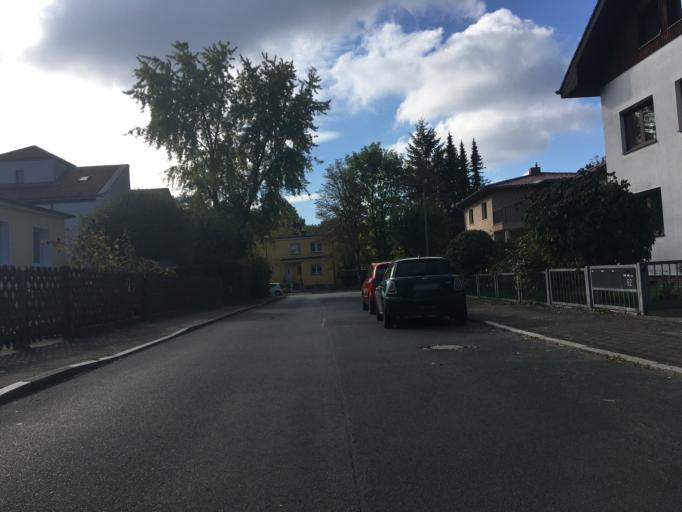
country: DE
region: Berlin
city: Britz
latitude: 52.4343
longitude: 13.4100
